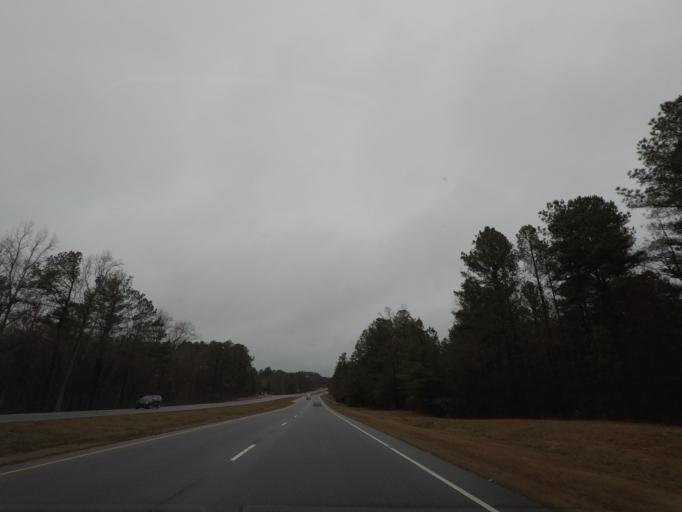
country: US
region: North Carolina
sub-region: Lee County
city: Broadway
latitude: 35.3236
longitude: -79.0921
